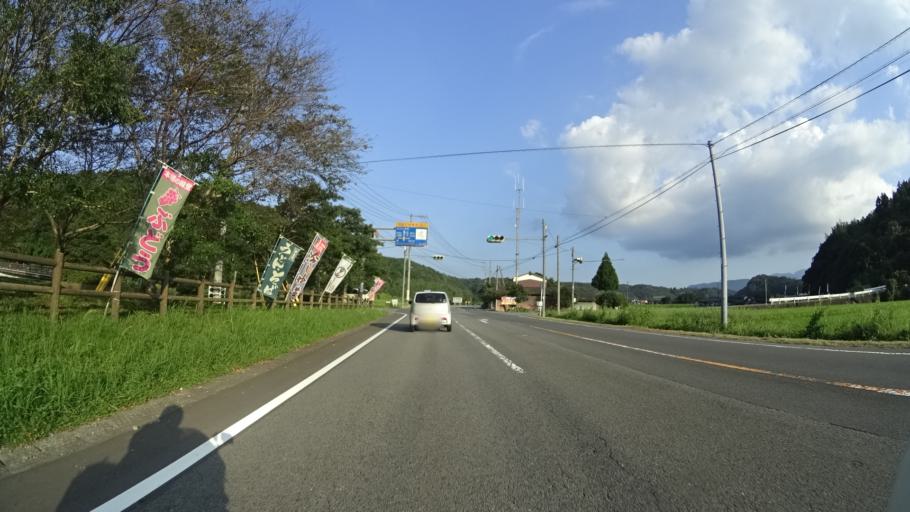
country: JP
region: Oita
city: Bungo-Takada-shi
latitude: 33.4239
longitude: 131.3755
